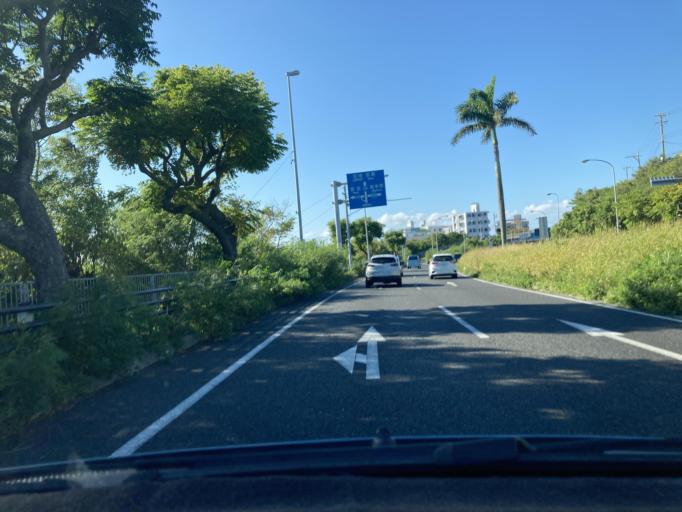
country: JP
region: Okinawa
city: Ginowan
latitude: 26.2498
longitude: 127.7430
